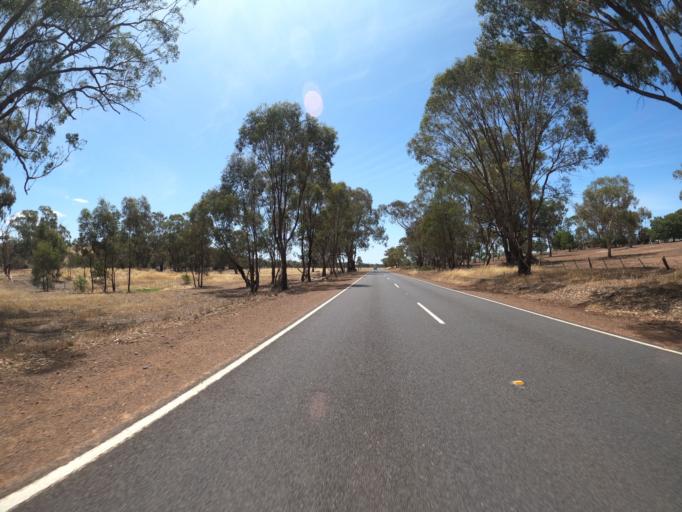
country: AU
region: Victoria
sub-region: Benalla
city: Benalla
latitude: -36.3339
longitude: 145.9598
